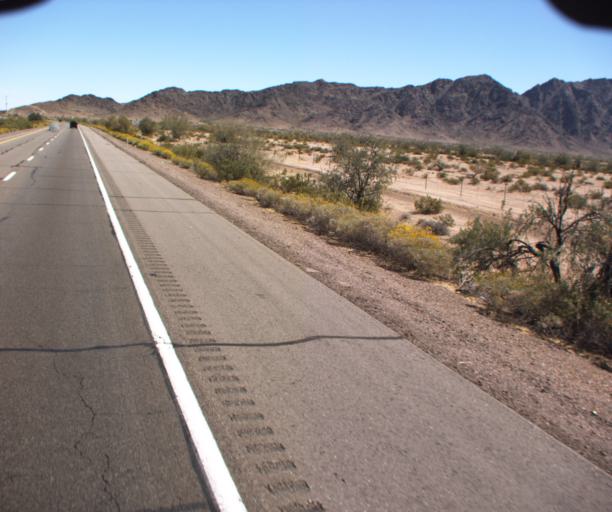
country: US
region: Arizona
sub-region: Yuma County
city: Wellton
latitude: 32.7216
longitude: -113.7670
